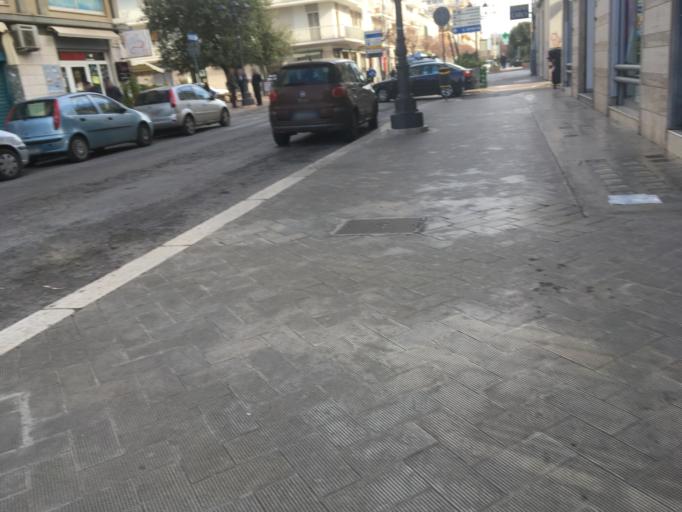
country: IT
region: Apulia
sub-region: Provincia di Bari
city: Bitonto
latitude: 41.1108
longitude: 16.6941
